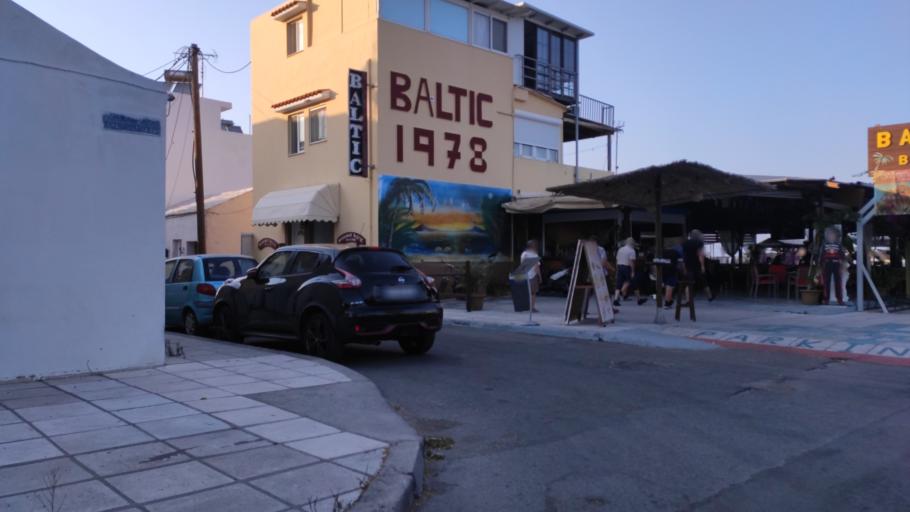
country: GR
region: South Aegean
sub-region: Nomos Dodekanisou
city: Kos
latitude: 36.9016
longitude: 27.2850
